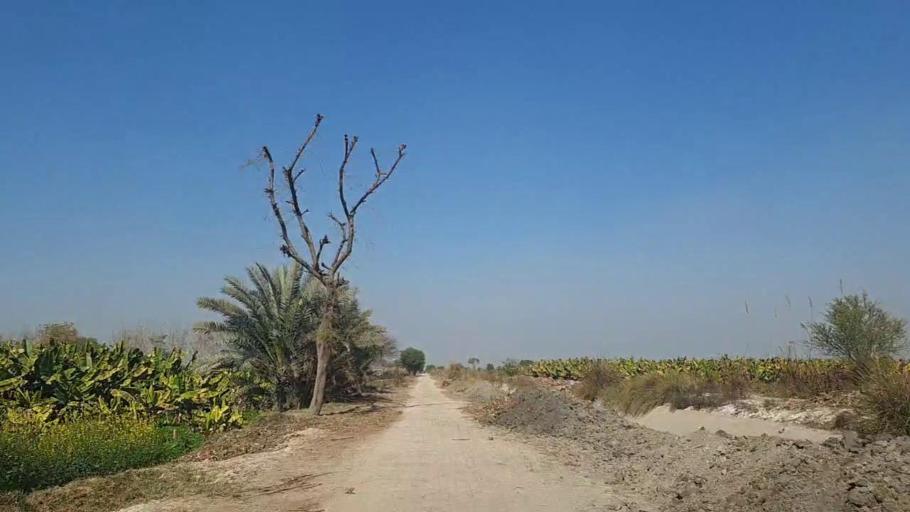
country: PK
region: Sindh
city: Sakrand
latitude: 26.2635
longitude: 68.2209
